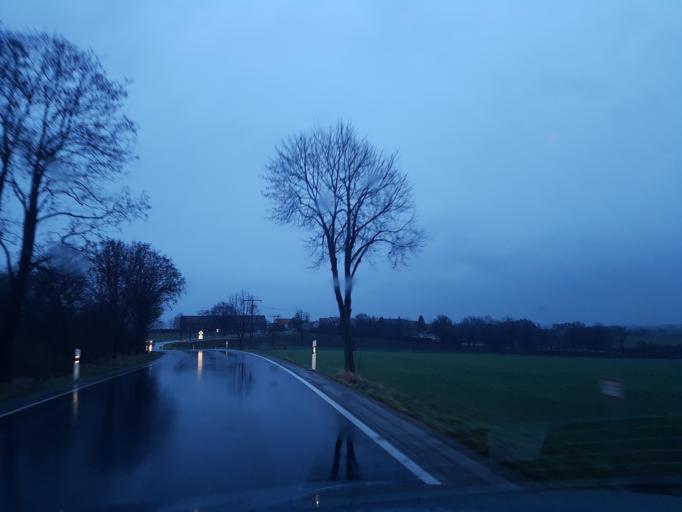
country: DE
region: Saxony
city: Priestewitz
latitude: 51.2519
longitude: 13.5191
